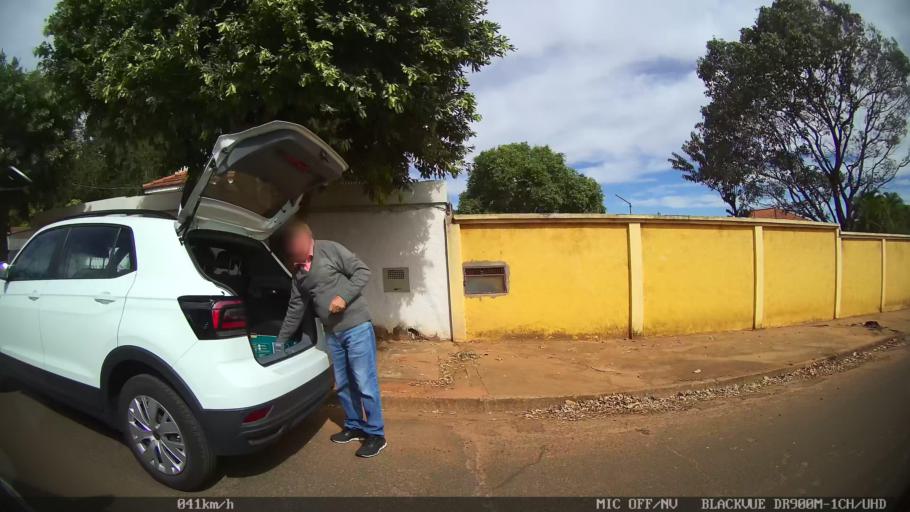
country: BR
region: Sao Paulo
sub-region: Catanduva
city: Catanduva
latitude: -21.1593
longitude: -48.9762
